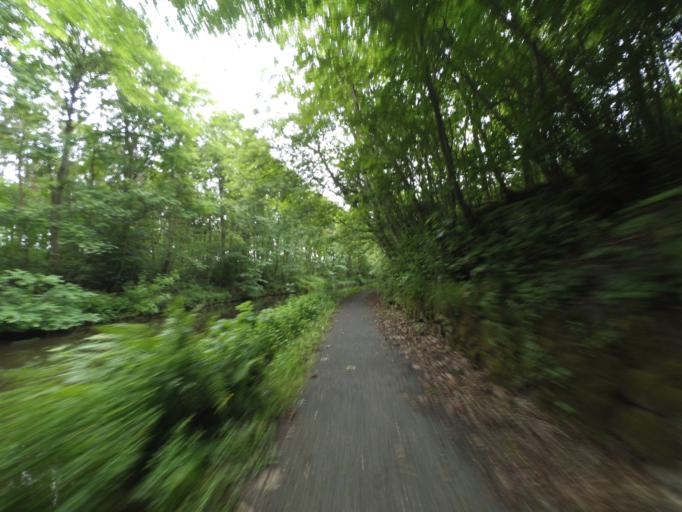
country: GB
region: Scotland
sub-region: West Lothian
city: Broxburn
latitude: 55.9716
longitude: -3.4871
